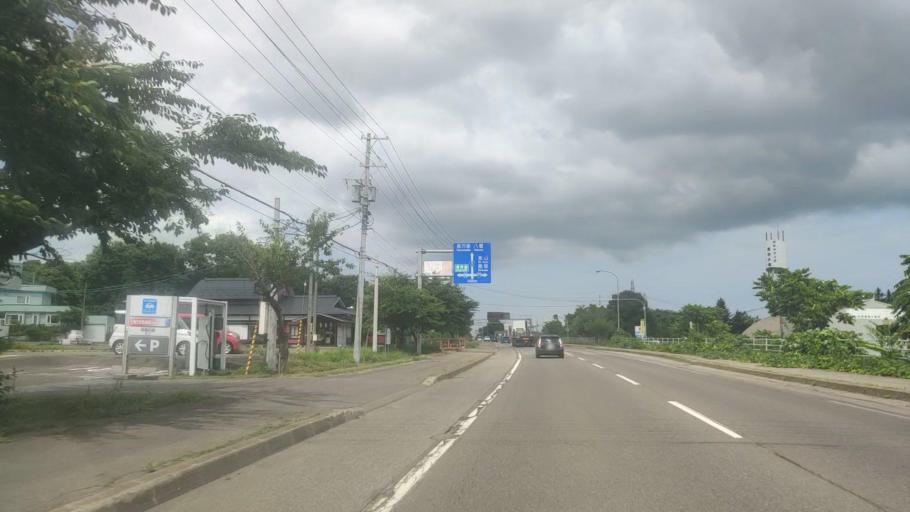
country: JP
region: Hokkaido
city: Nanae
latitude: 42.0897
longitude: 140.5809
